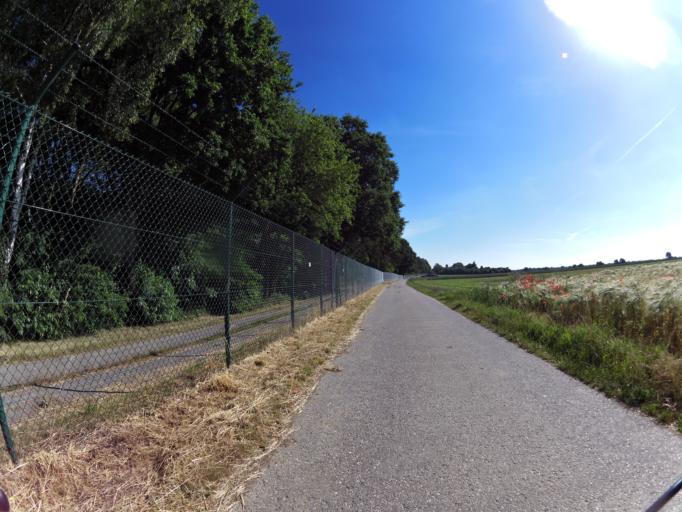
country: DE
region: North Rhine-Westphalia
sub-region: Regierungsbezirk Koln
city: Ubach-Palenberg
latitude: 50.9490
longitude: 6.0518
